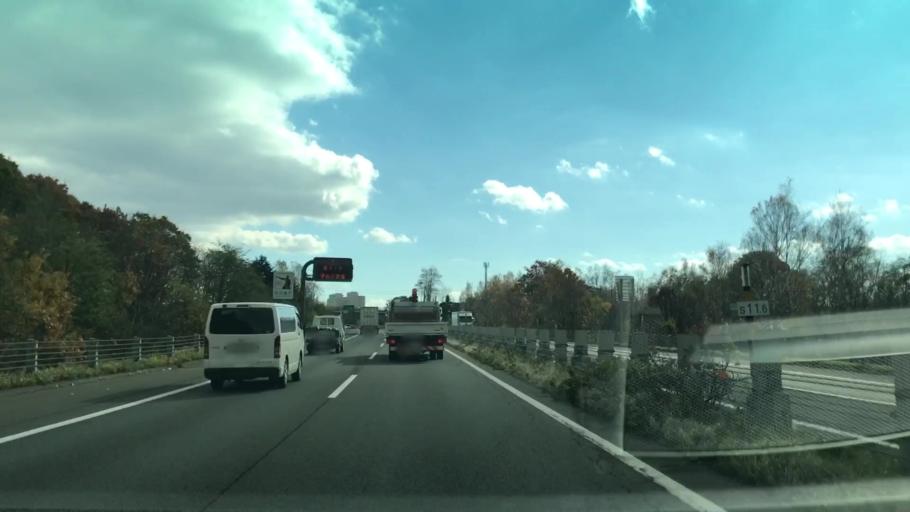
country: JP
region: Hokkaido
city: Kitahiroshima
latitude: 42.9827
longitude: 141.4731
